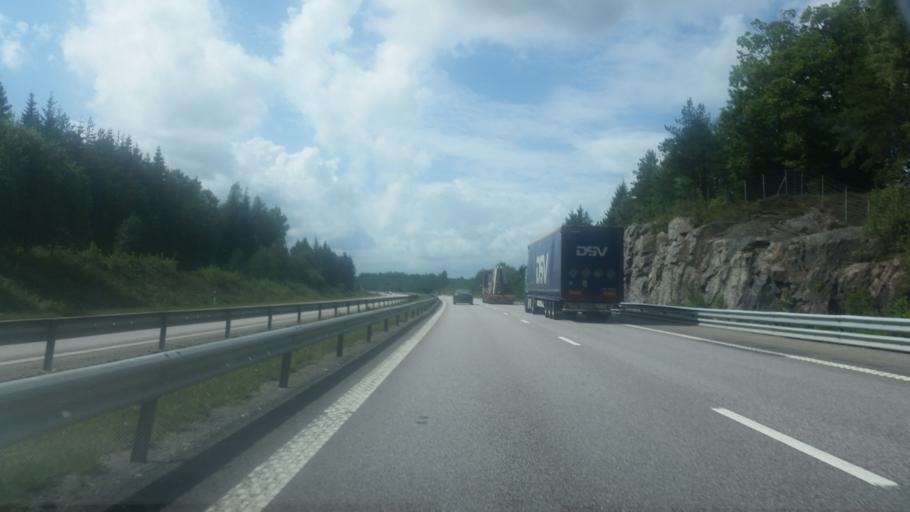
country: SE
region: Vaestra Goetaland
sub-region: Boras Kommun
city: Sandared
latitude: 57.6806
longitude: 12.7132
